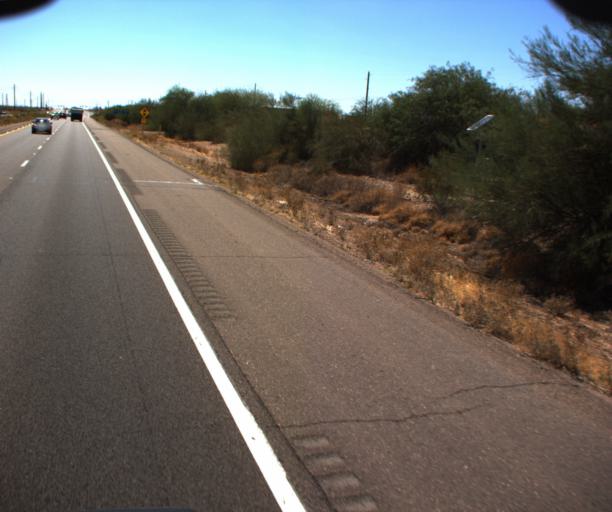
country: US
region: Arizona
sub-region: Maricopa County
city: Mesa
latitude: 33.5060
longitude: -111.7808
